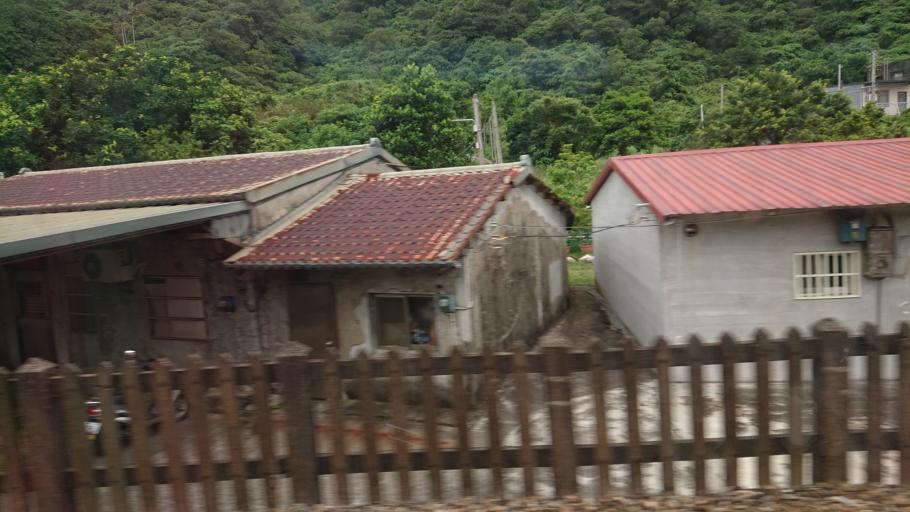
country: TW
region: Taiwan
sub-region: Yilan
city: Yilan
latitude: 24.9227
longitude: 121.8828
